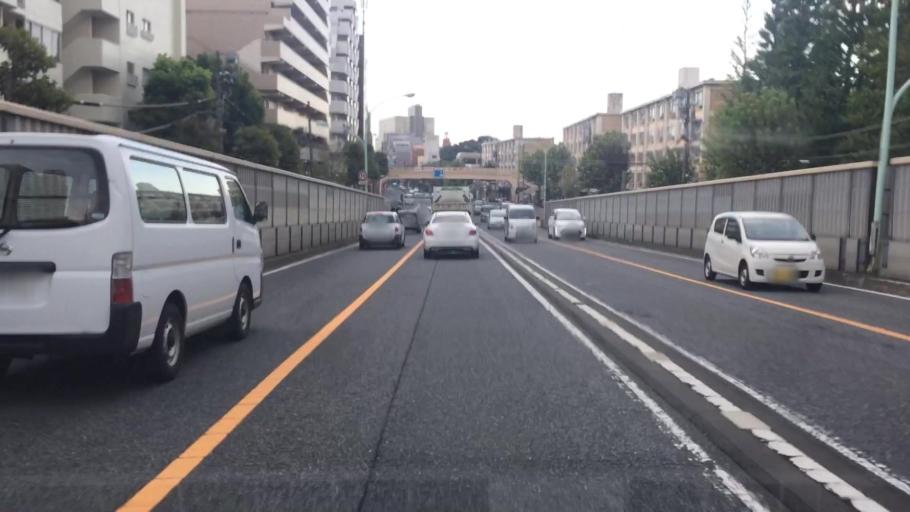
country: JP
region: Tokyo
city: Tokyo
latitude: 35.6971
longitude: 139.6546
